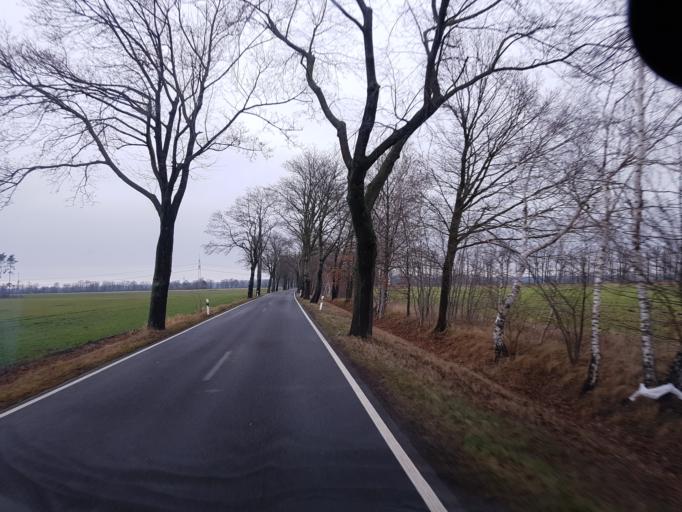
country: DE
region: Brandenburg
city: Plessa
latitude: 51.4368
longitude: 13.6243
